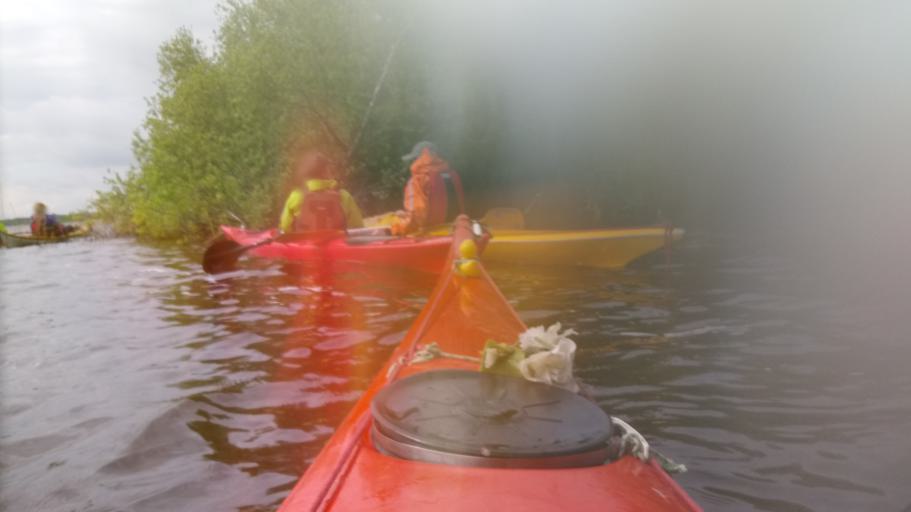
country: NL
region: Overijssel
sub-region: Gemeente Steenwijkerland
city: Sint Jansklooster
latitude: 52.6944
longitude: 6.0237
